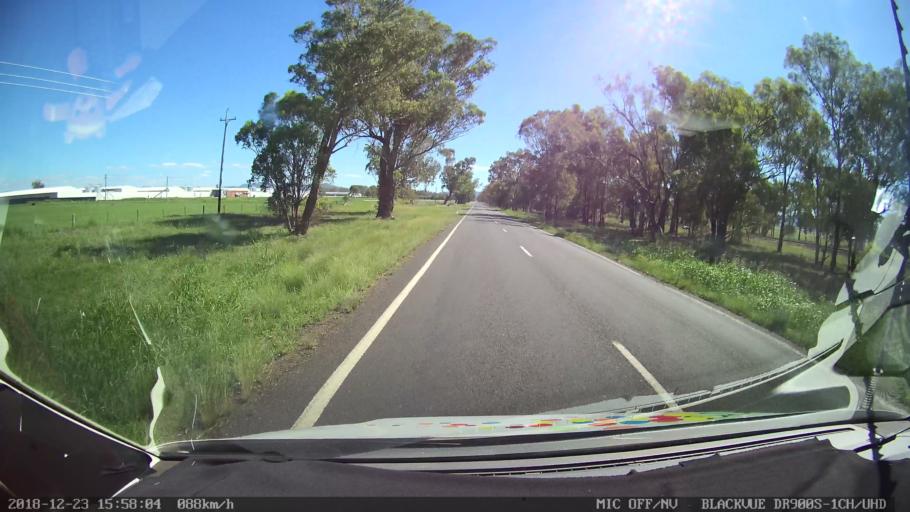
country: AU
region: New South Wales
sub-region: Tamworth Municipality
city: Phillip
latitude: -31.1842
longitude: 150.8447
